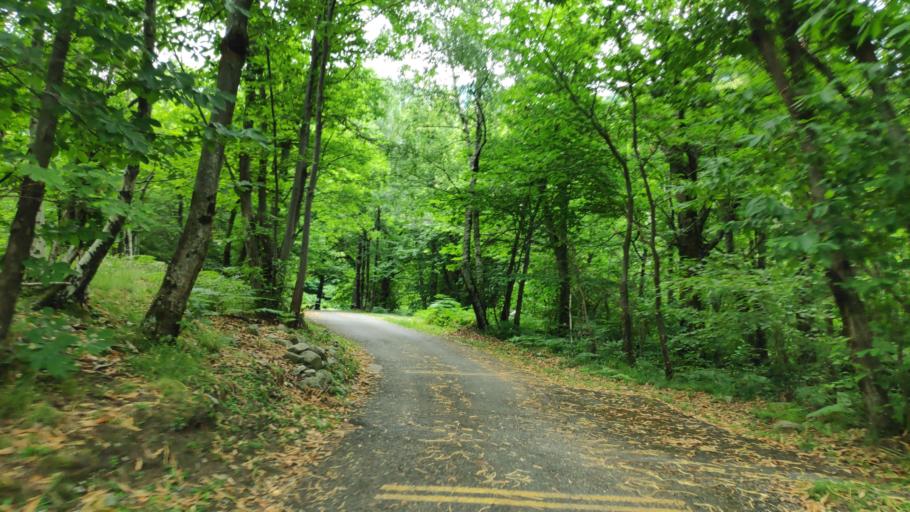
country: IT
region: Lombardy
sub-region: Provincia di Sondrio
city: Prata Centro
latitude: 46.2993
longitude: 9.4078
